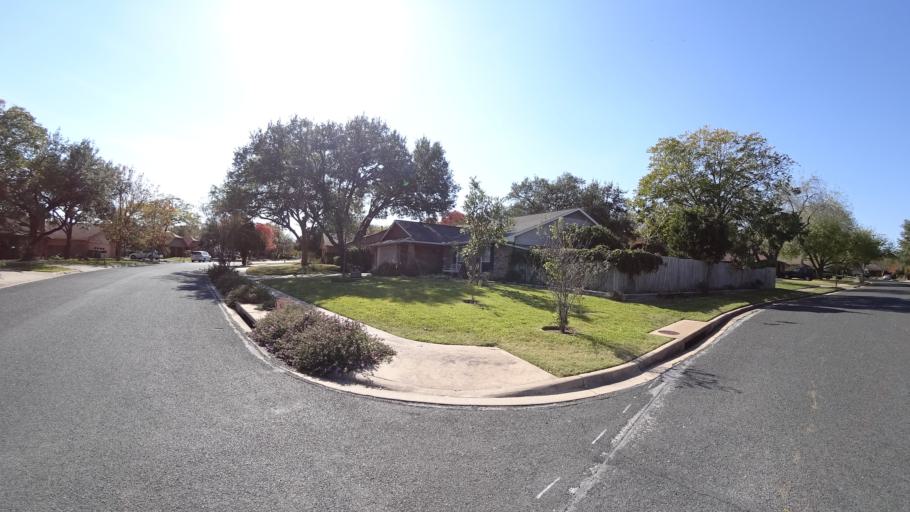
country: US
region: Texas
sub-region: Travis County
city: Shady Hollow
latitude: 30.2229
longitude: -97.8576
